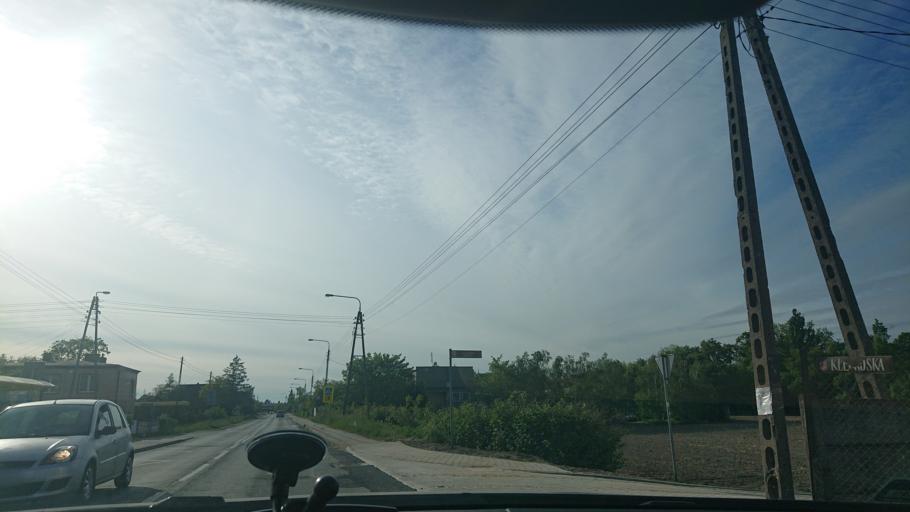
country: PL
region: Greater Poland Voivodeship
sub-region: Powiat gnieznienski
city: Gniezno
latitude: 52.5417
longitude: 17.5780
